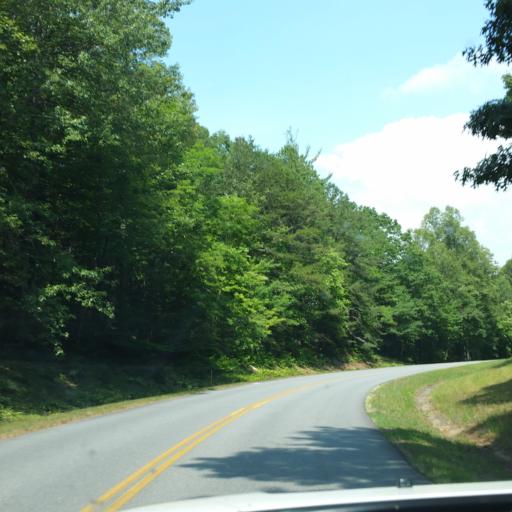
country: US
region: North Carolina
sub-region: Buncombe County
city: Avery Creek
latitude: 35.4961
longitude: -82.5665
